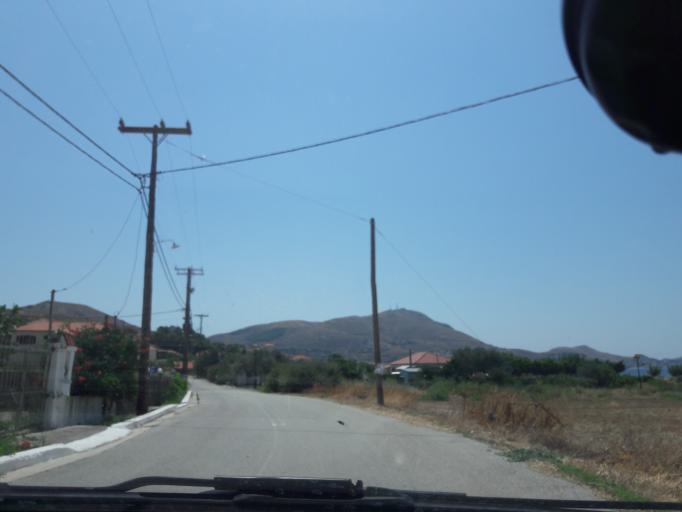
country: GR
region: North Aegean
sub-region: Nomos Lesvou
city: Myrina
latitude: 39.9304
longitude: 25.0644
